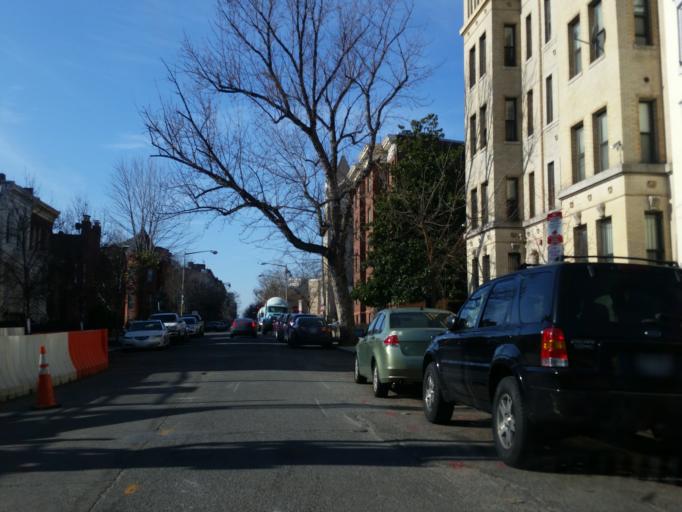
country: US
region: Washington, D.C.
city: Washington, D.C.
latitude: 38.9073
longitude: -77.0251
